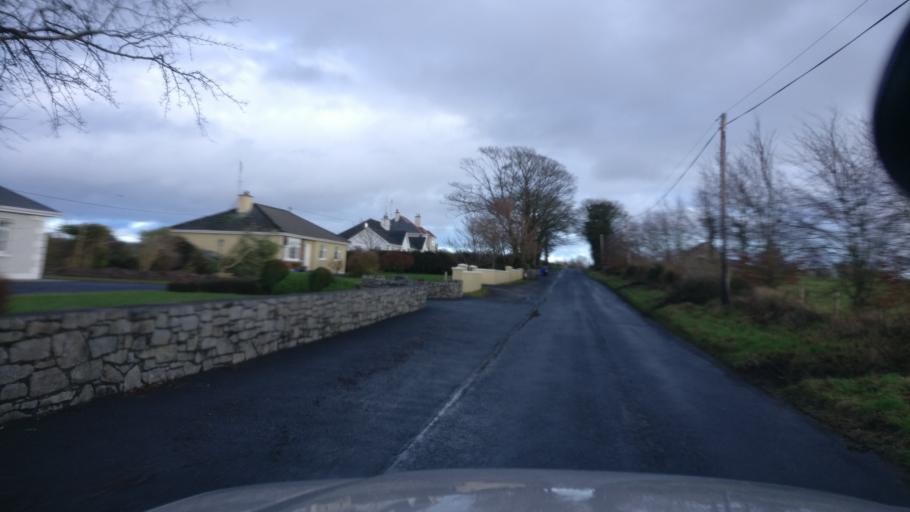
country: IE
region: Connaught
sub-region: County Galway
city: Athenry
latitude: 53.2956
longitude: -8.6919
